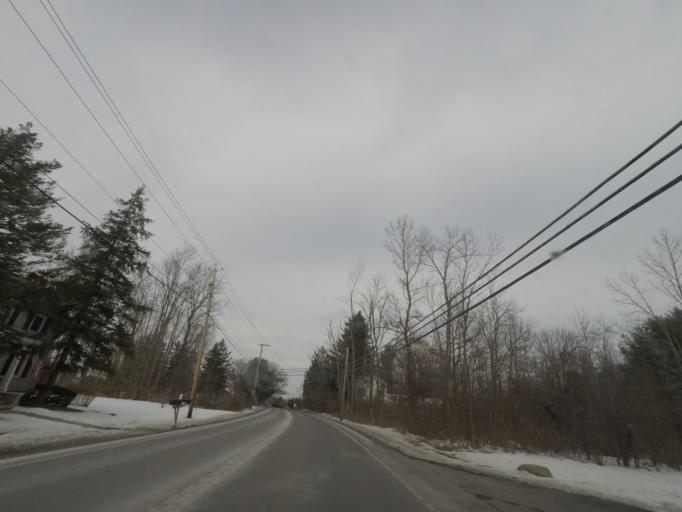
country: US
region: New York
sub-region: Albany County
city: Voorheesville
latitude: 42.5911
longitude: -73.9118
